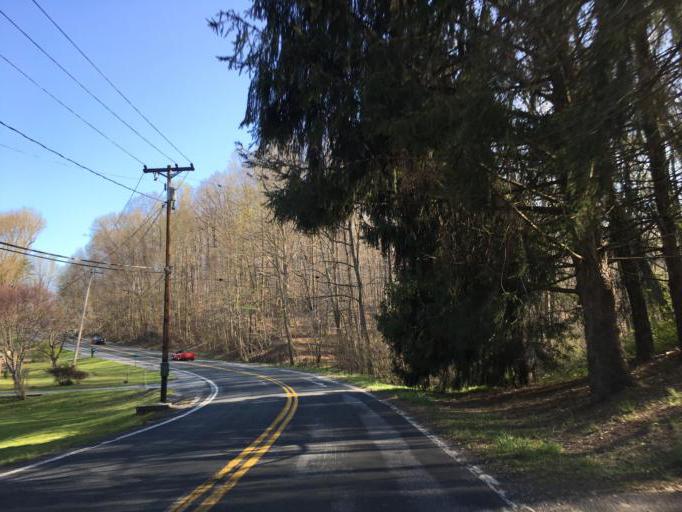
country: US
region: Maryland
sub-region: Baltimore County
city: Perry Hall
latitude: 39.4666
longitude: -76.4908
